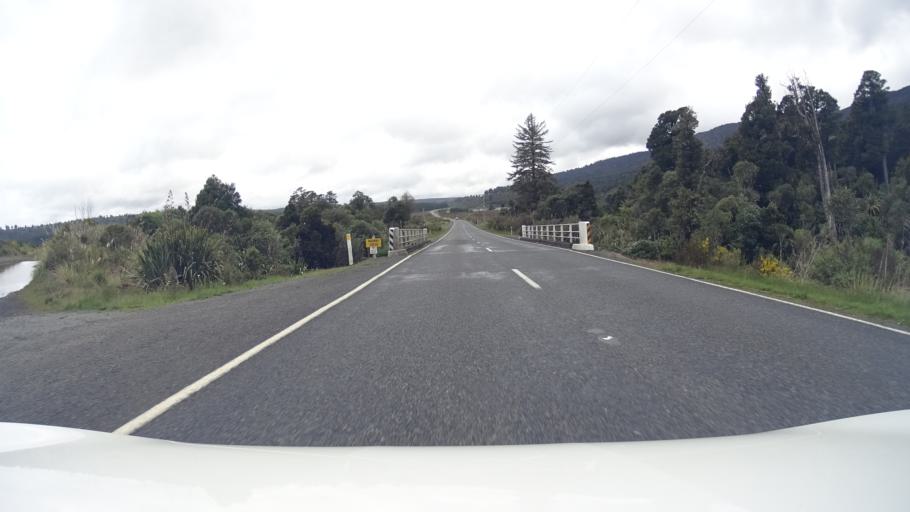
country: NZ
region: Manawatu-Wanganui
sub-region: Ruapehu District
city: Waiouru
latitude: -39.2351
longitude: 175.3921
